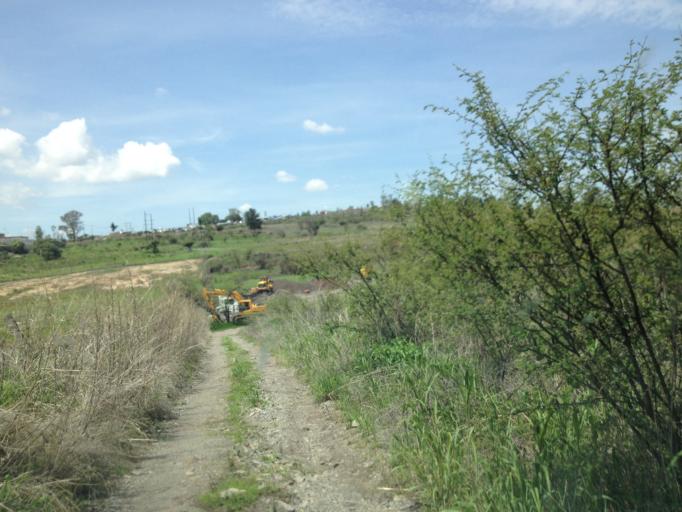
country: MX
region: Michoacan
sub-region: Tarimbaro
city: San Bernabe de las Canteras
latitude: 19.7650
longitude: -101.1667
